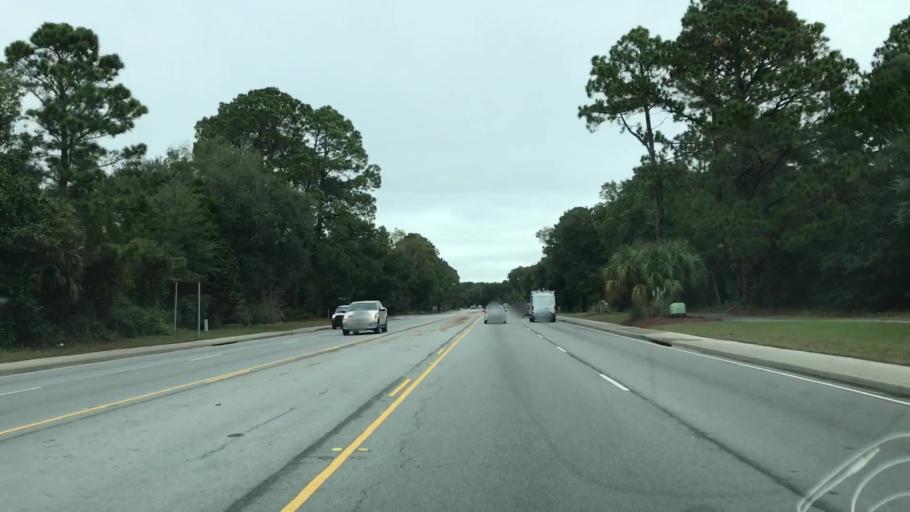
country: US
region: South Carolina
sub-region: Beaufort County
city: Hilton Head Island
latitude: 32.1947
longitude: -80.7050
